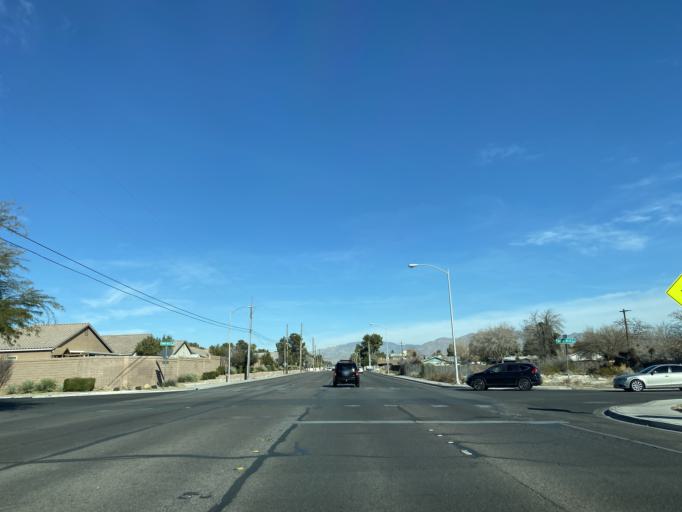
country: US
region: Nevada
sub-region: Clark County
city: Las Vegas
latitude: 36.2080
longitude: -115.2244
